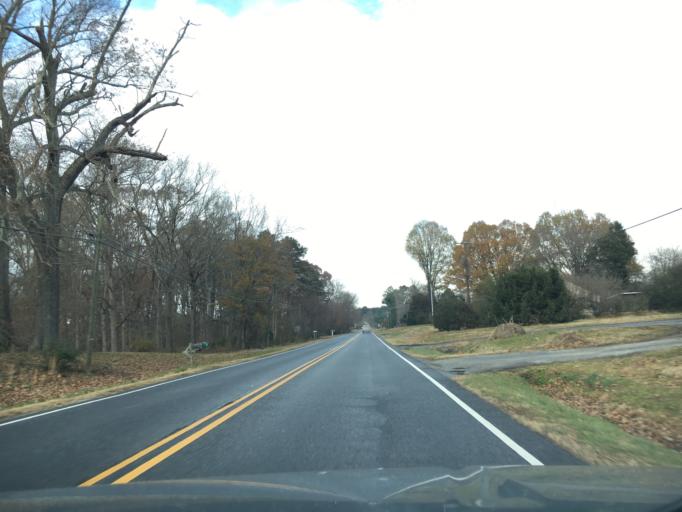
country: US
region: Virginia
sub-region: Prince Edward County
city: Farmville
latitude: 37.3217
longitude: -78.3862
